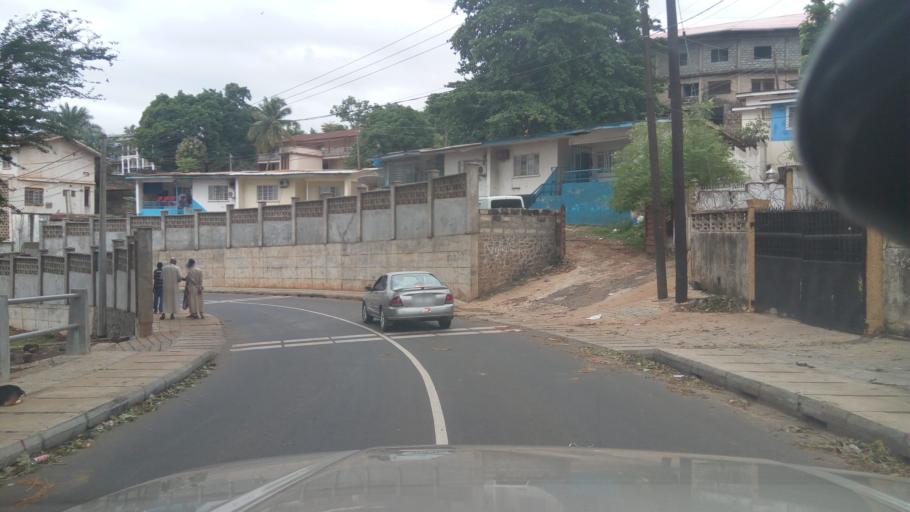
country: SL
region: Western Area
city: Freetown
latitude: 8.4821
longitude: -13.2642
